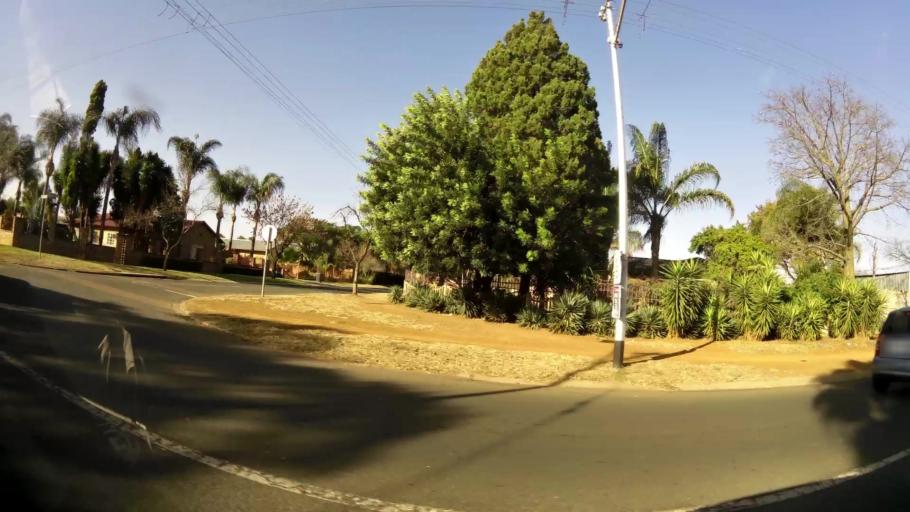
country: ZA
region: Gauteng
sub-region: City of Tshwane Metropolitan Municipality
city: Pretoria
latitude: -25.7107
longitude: 28.2425
